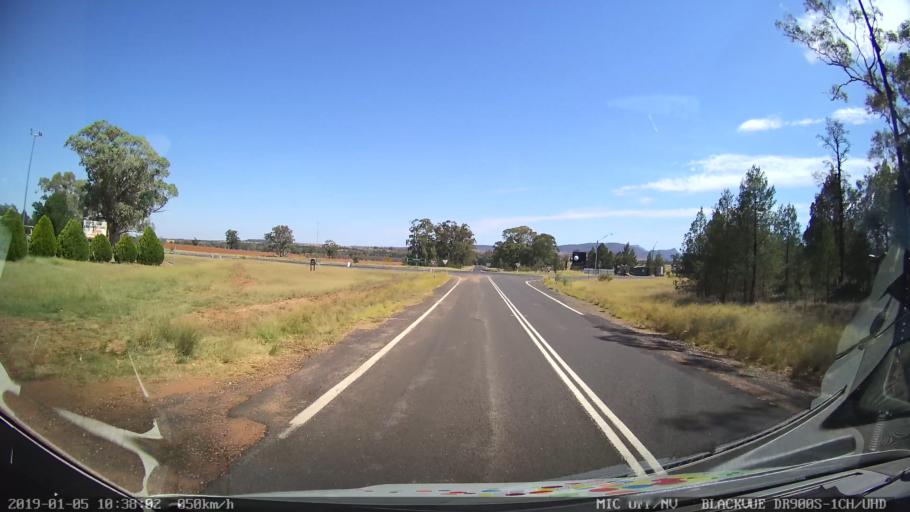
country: AU
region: New South Wales
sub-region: Gilgandra
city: Gilgandra
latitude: -31.4704
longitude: 148.9203
